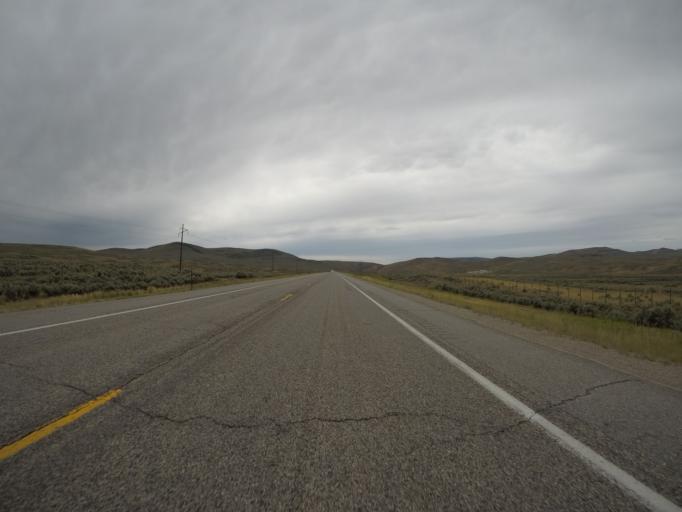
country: US
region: Wyoming
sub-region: Lincoln County
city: Kemmerer
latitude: 41.8170
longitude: -110.7757
